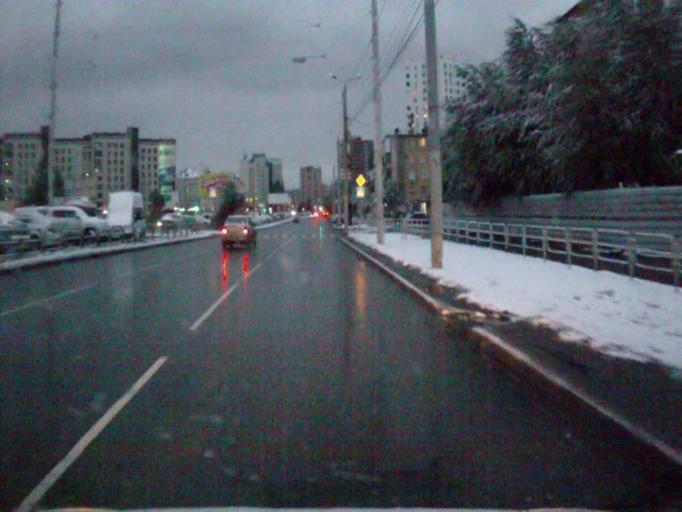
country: RU
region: Chelyabinsk
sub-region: Gorod Chelyabinsk
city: Chelyabinsk
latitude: 55.1485
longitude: 61.3935
